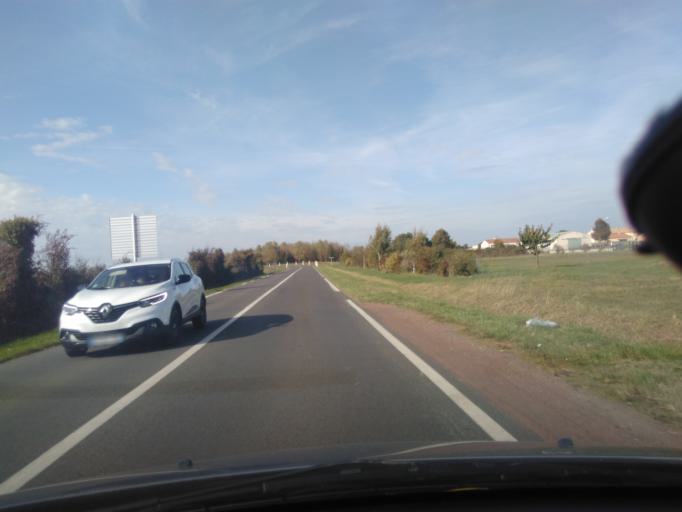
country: FR
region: Pays de la Loire
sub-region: Departement de la Vendee
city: Jard-sur-Mer
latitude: 46.4264
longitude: -1.5749
